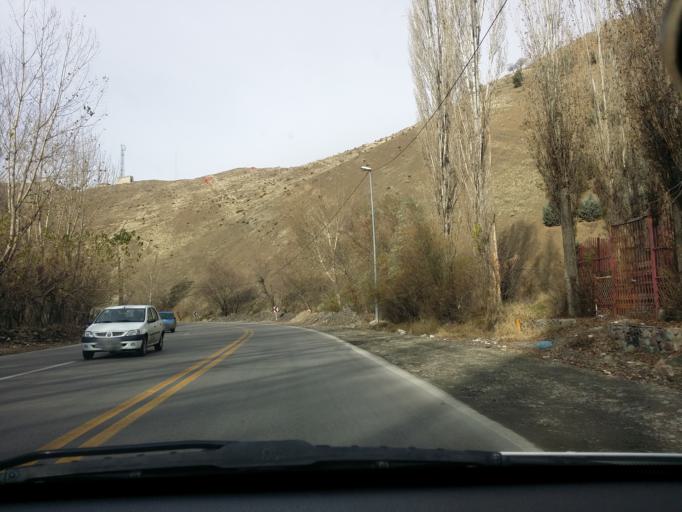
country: IR
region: Alborz
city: Karaj
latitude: 36.0352
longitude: 51.2019
